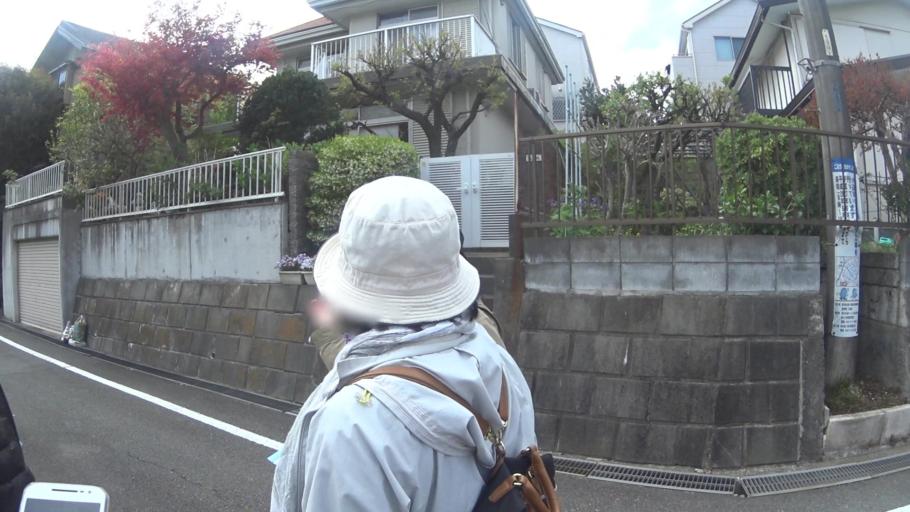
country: JP
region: Tokyo
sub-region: Machida-shi
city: Machida
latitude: 35.5745
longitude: 139.4723
